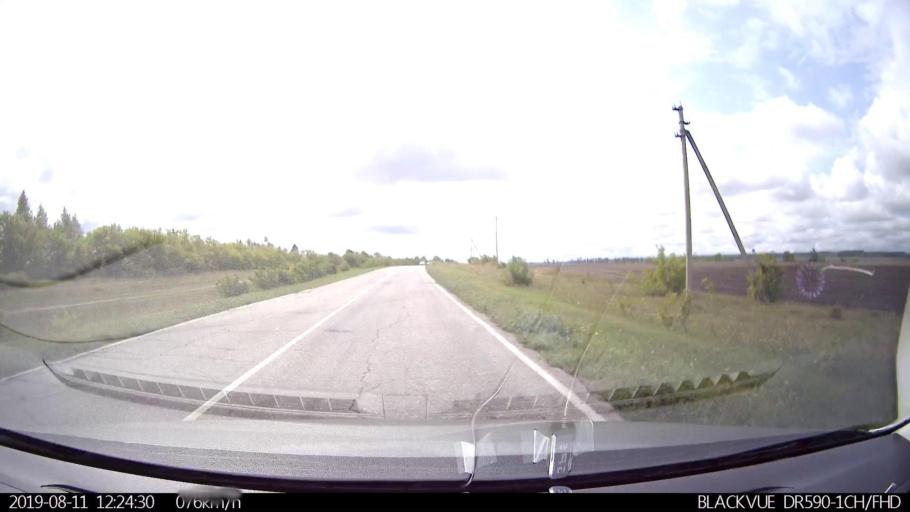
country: RU
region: Ulyanovsk
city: Ignatovka
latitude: 53.8827
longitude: 47.9482
